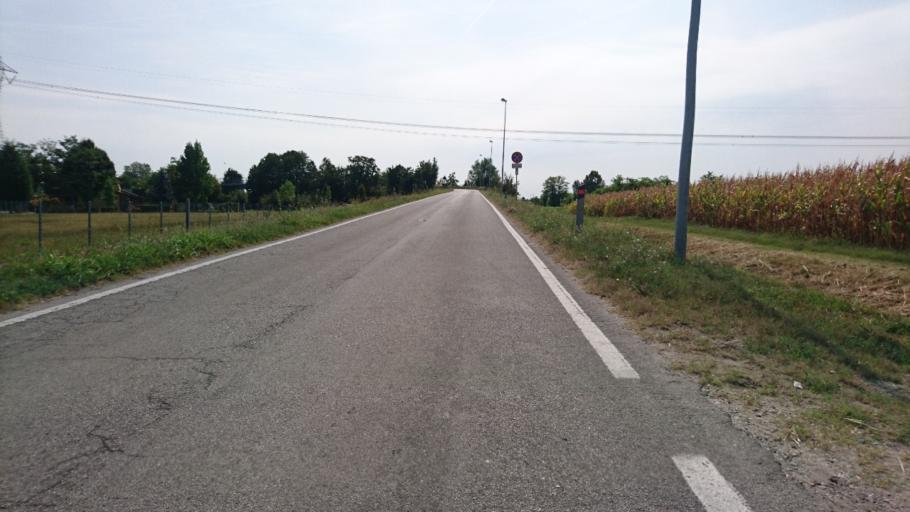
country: IT
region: Veneto
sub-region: Provincia di Padova
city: Mandriola-Sant'Agostino
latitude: 45.3612
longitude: 11.8534
